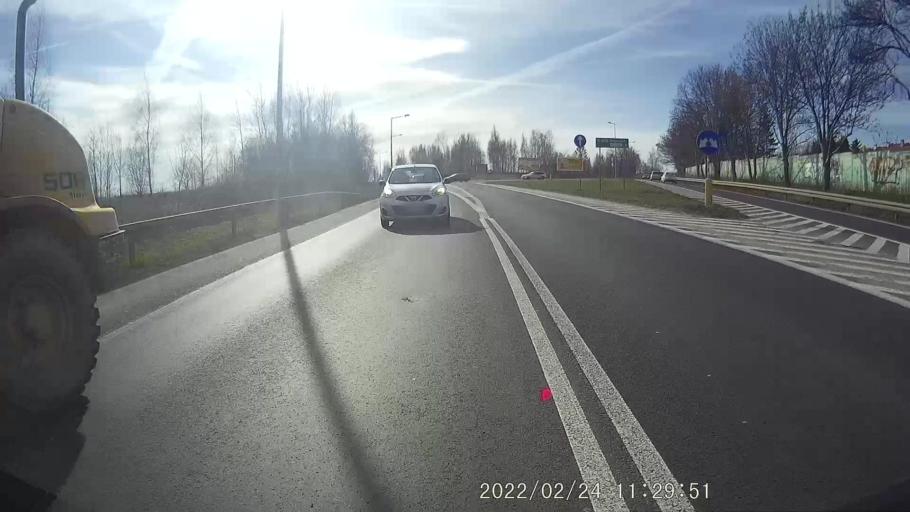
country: PL
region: Lower Silesian Voivodeship
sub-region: Powiat polkowicki
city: Przemkow
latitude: 51.5226
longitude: 15.7138
